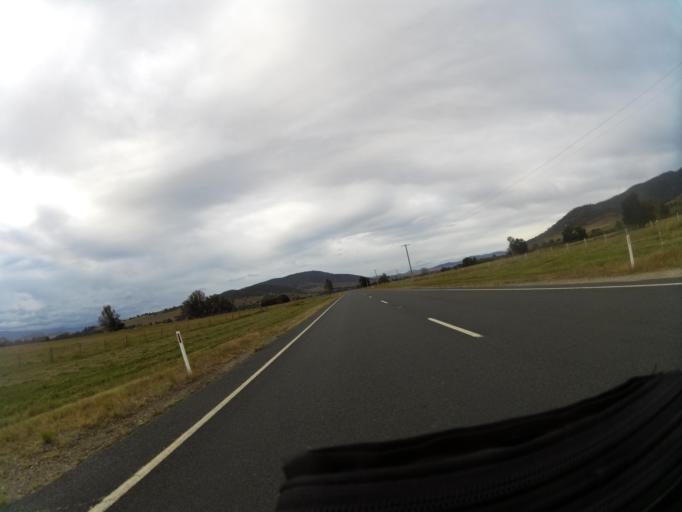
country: AU
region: New South Wales
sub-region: Snowy River
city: Jindabyne
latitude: -36.1094
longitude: 147.9796
